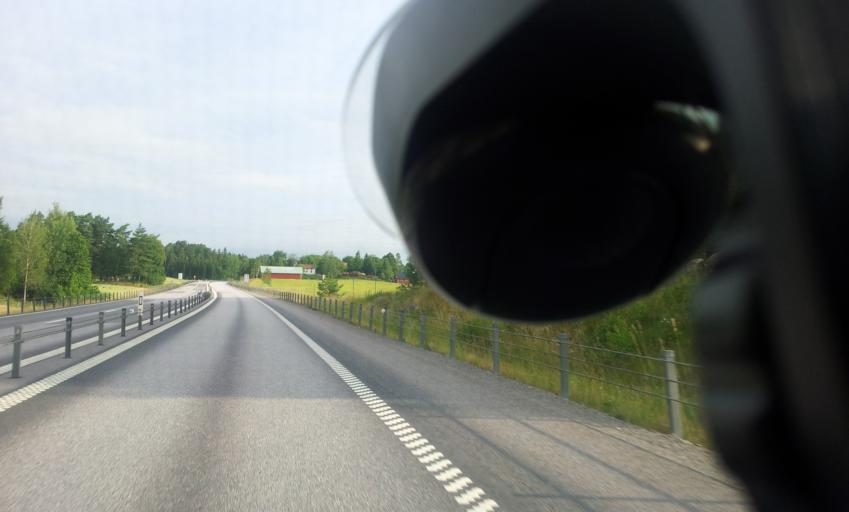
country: SE
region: OEstergoetland
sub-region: Valdemarsviks Kommun
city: Gusum
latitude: 58.3030
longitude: 16.4910
